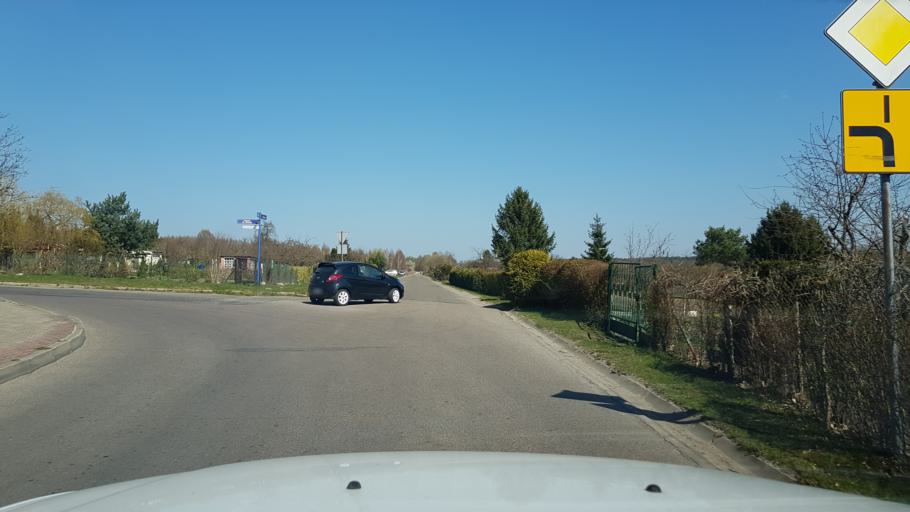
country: PL
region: West Pomeranian Voivodeship
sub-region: Powiat slawienski
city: Slawno
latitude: 54.3696
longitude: 16.6894
